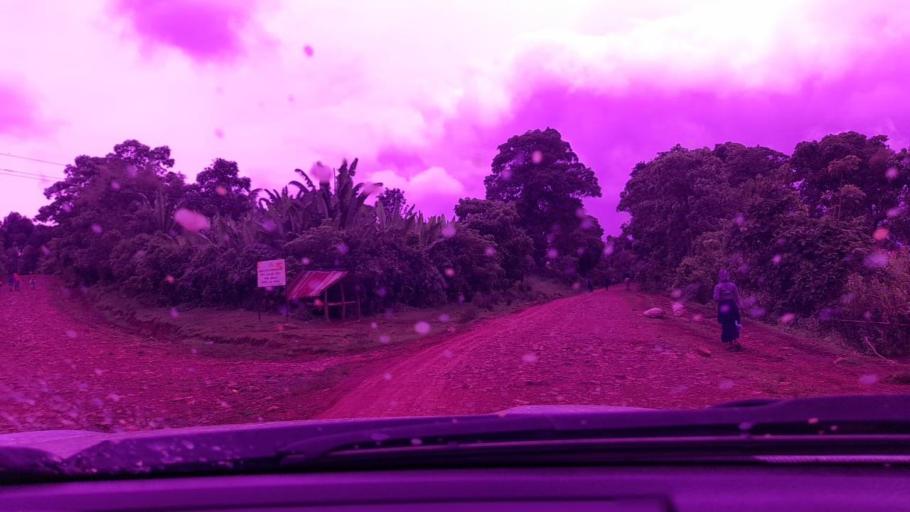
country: ET
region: Southern Nations, Nationalities, and People's Region
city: Tippi
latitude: 7.5721
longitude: 35.6449
